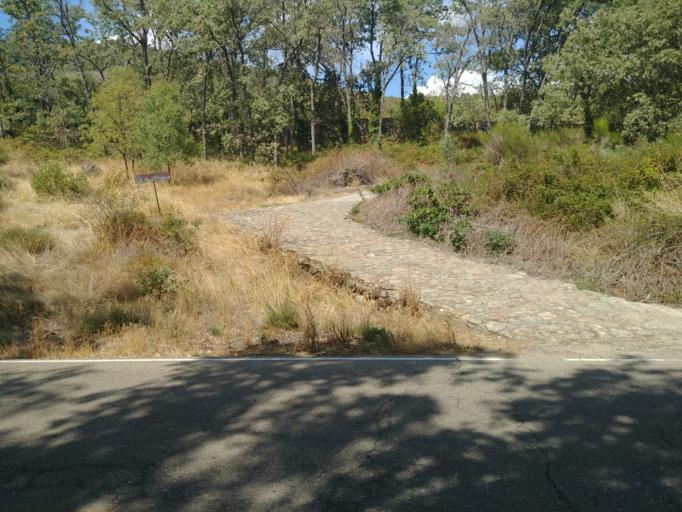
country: ES
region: Extremadura
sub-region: Provincia de Caceres
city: Aldeanueva de la Vera
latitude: 40.1115
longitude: -5.7354
